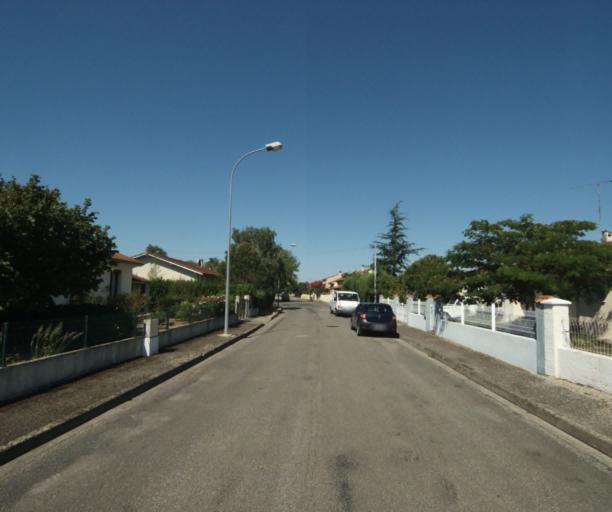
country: FR
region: Midi-Pyrenees
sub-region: Departement de la Haute-Garonne
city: Revel
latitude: 43.4583
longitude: 2.0174
